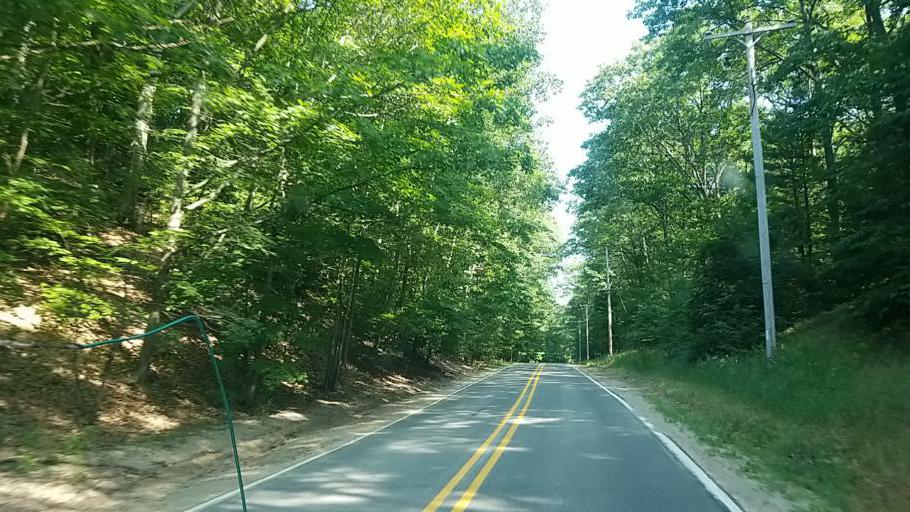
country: US
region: Michigan
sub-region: Muskegon County
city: Whitehall
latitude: 43.3303
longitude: -86.3996
